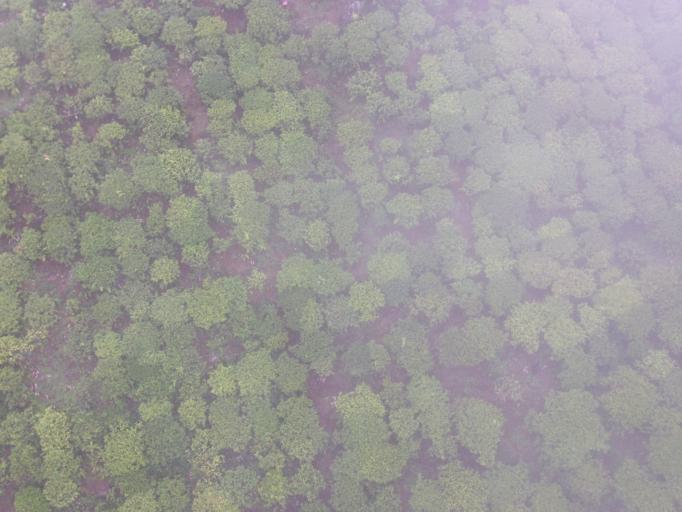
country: IN
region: West Bengal
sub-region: Darjiling
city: Darjiling
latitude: 27.0680
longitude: 88.2544
